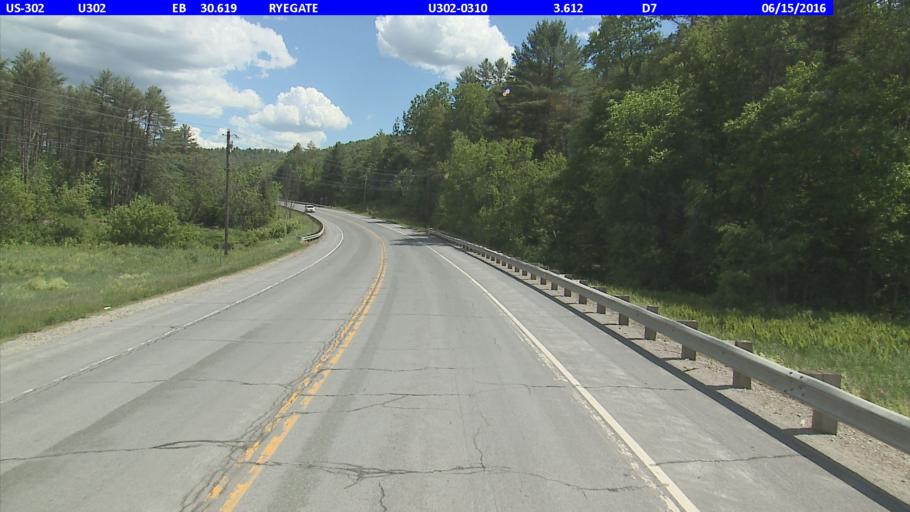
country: US
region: New Hampshire
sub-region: Grafton County
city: Woodsville
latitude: 44.1783
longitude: -72.1178
